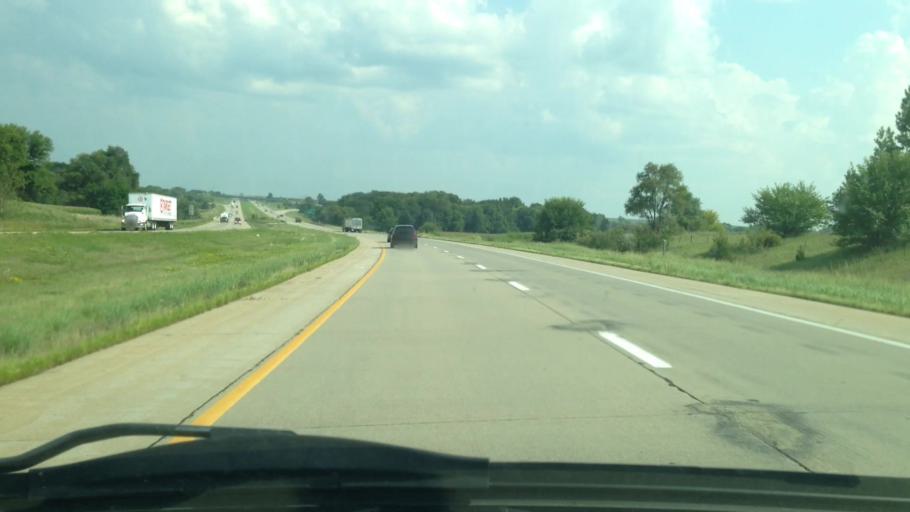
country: US
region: Iowa
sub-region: Black Hawk County
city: Elk Run Heights
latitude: 42.4224
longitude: -92.1840
